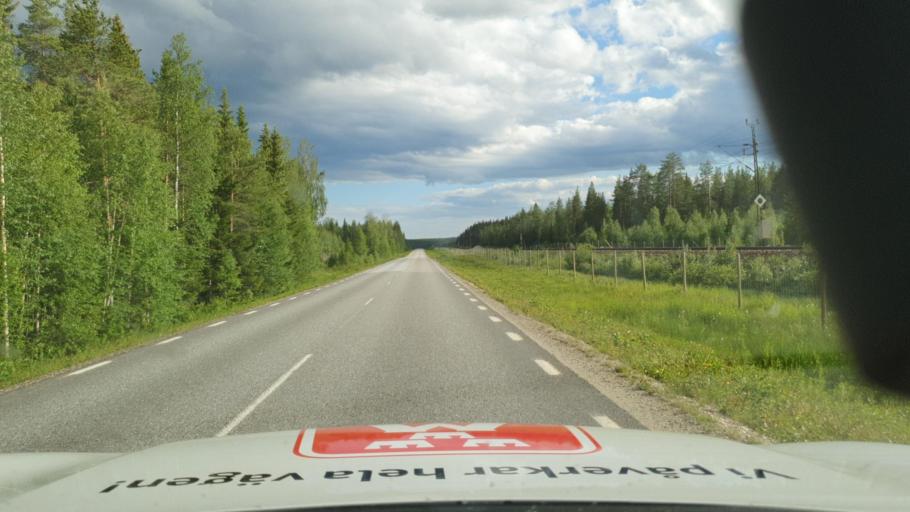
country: SE
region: Vaesterbotten
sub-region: Vindelns Kommun
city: Vindeln
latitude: 64.3770
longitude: 19.6586
